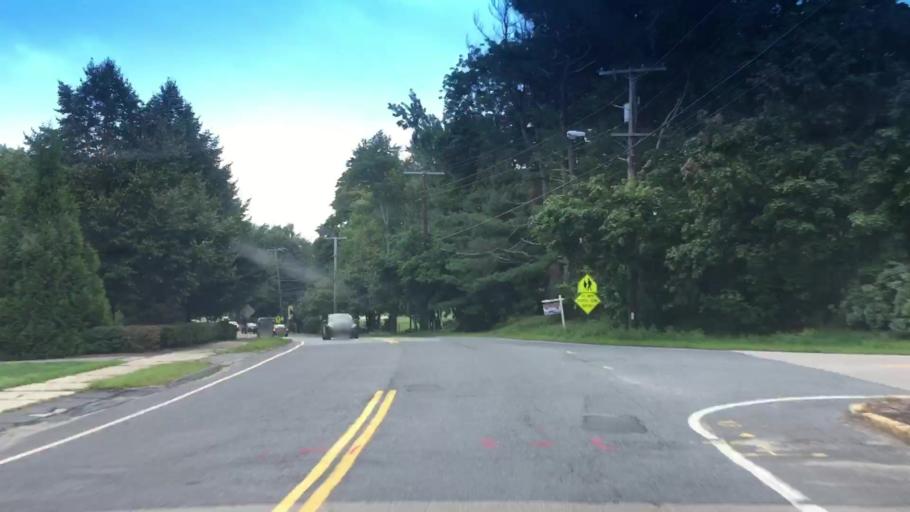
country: US
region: Massachusetts
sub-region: Norfolk County
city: Walpole
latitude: 42.1480
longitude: -71.2407
